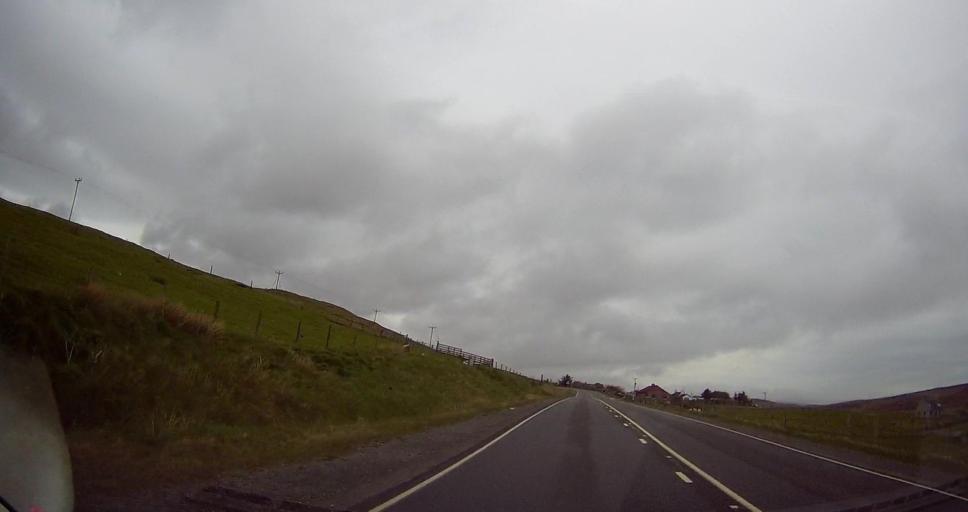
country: GB
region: Scotland
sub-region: Shetland Islands
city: Lerwick
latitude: 60.2380
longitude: -1.2300
